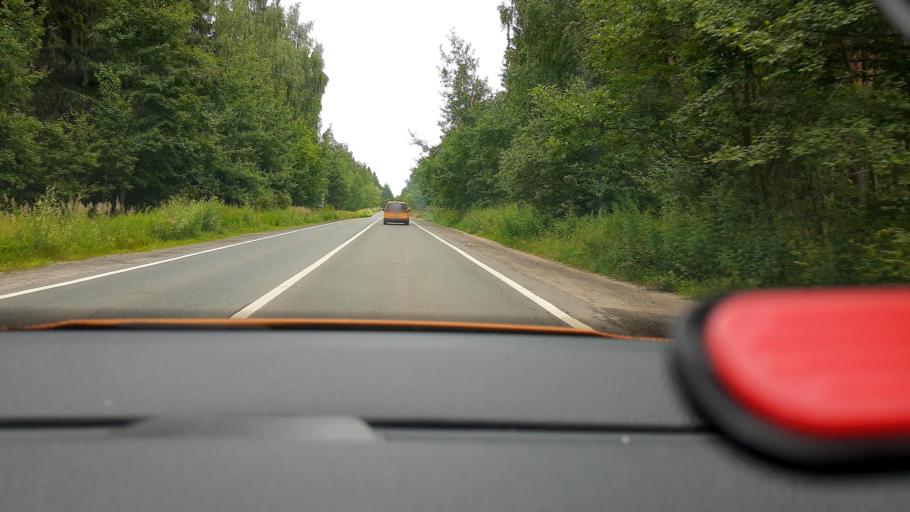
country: RU
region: Moskovskaya
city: Pirogovskiy
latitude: 55.9978
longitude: 37.6761
